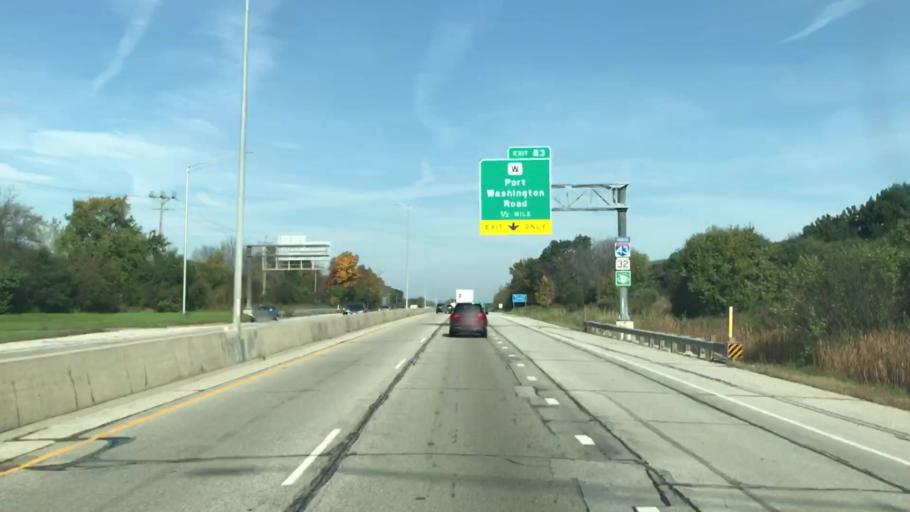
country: US
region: Wisconsin
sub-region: Milwaukee County
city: River Hills
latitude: 43.1790
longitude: -87.9182
